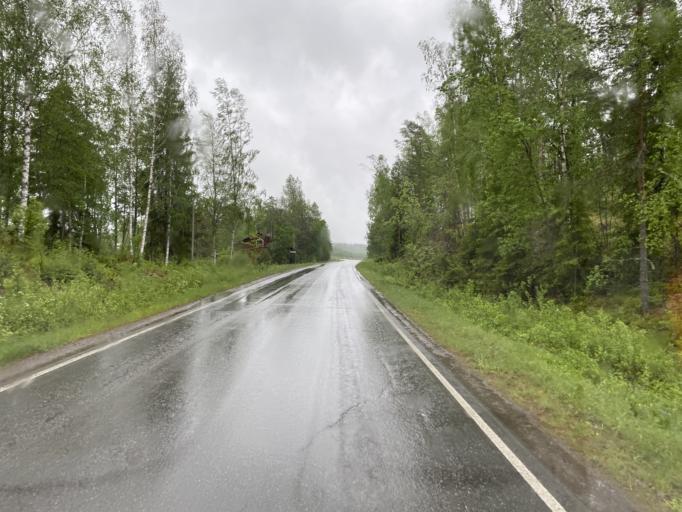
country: FI
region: Pirkanmaa
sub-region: Etelae-Pirkanmaa
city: Urjala
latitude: 61.0389
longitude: 23.4544
